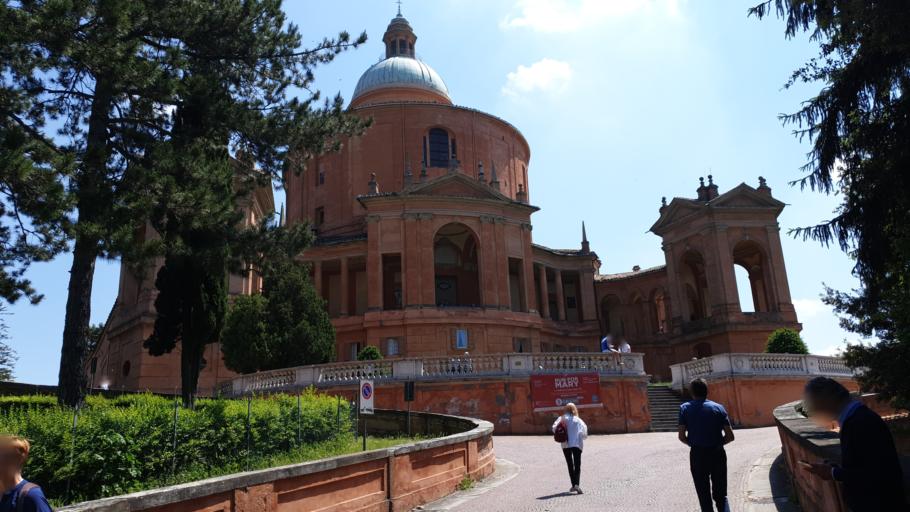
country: IT
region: Emilia-Romagna
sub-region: Provincia di Bologna
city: Casalecchio di Reno
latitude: 44.4793
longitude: 11.2971
